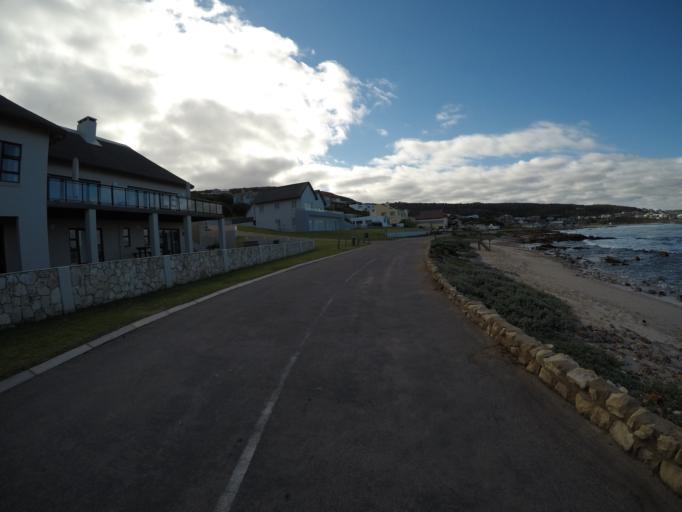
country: ZA
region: Western Cape
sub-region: Eden District Municipality
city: Riversdale
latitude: -34.4311
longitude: 21.3351
